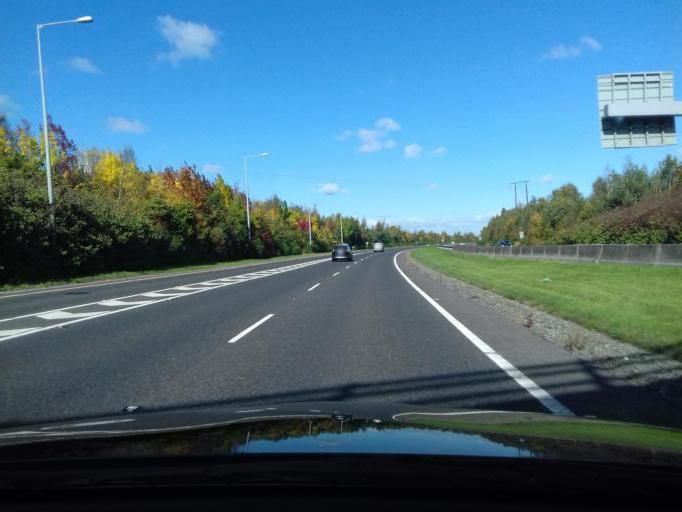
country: IE
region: Leinster
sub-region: Fingal County
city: Blanchardstown
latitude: 53.4386
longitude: -6.3539
